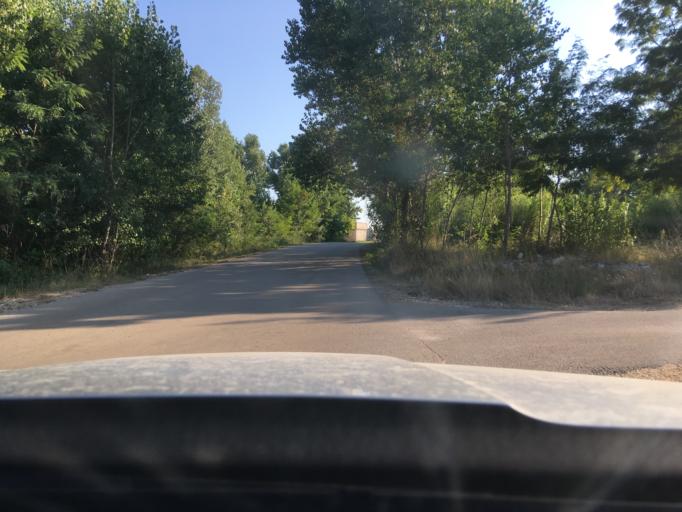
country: HR
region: Zadarska
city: Nin
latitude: 44.2533
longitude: 15.1553
